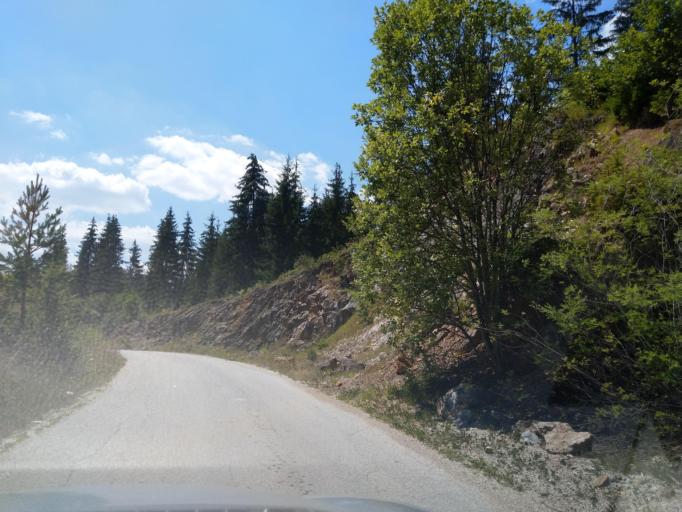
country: RS
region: Central Serbia
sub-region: Zlatiborski Okrug
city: Nova Varos
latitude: 43.4781
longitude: 19.9662
